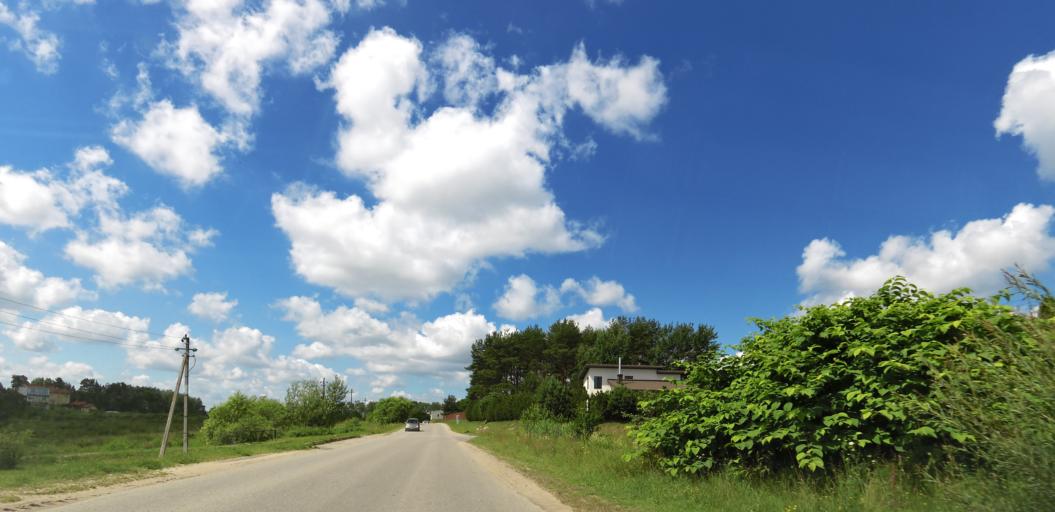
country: LT
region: Vilnius County
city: Pasilaiciai
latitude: 54.7359
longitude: 25.1990
